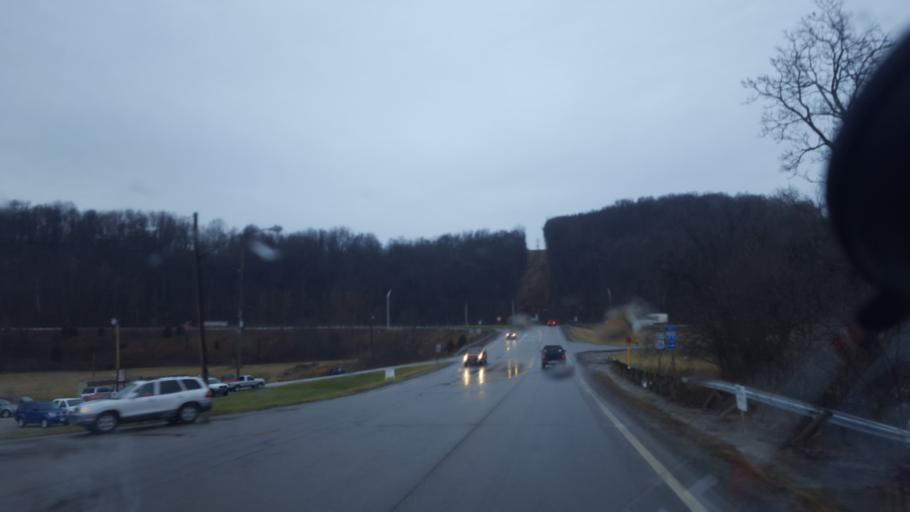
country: US
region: Ohio
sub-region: Tuscarawas County
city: Newcomerstown
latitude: 40.2786
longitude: -81.5912
